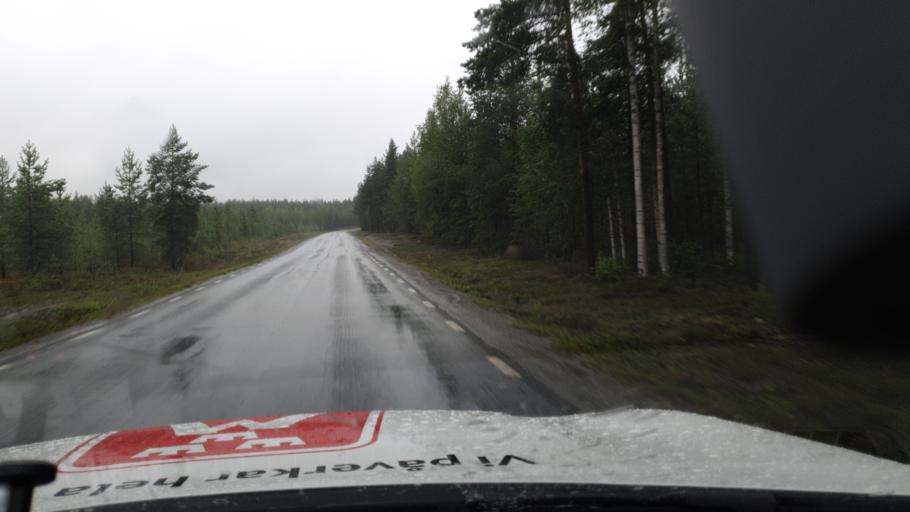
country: SE
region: Vaesterbotten
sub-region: Skelleftea Kommun
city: Burea
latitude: 64.6084
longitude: 21.1592
